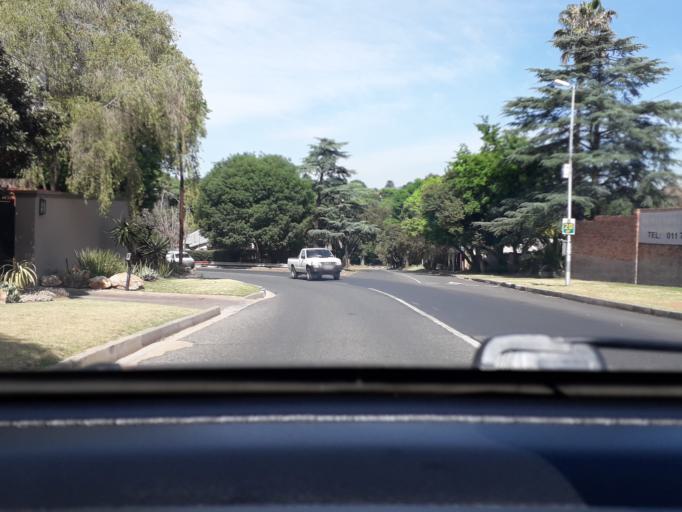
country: ZA
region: Gauteng
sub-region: City of Johannesburg Metropolitan Municipality
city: Johannesburg
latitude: -26.1430
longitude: 28.0736
